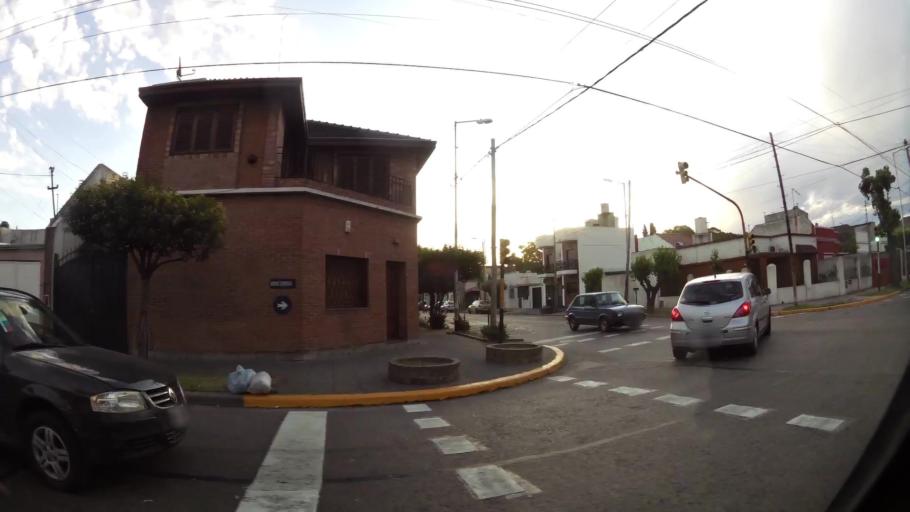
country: AR
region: Buenos Aires
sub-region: Partido de Avellaneda
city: Avellaneda
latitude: -34.7044
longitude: -58.3349
